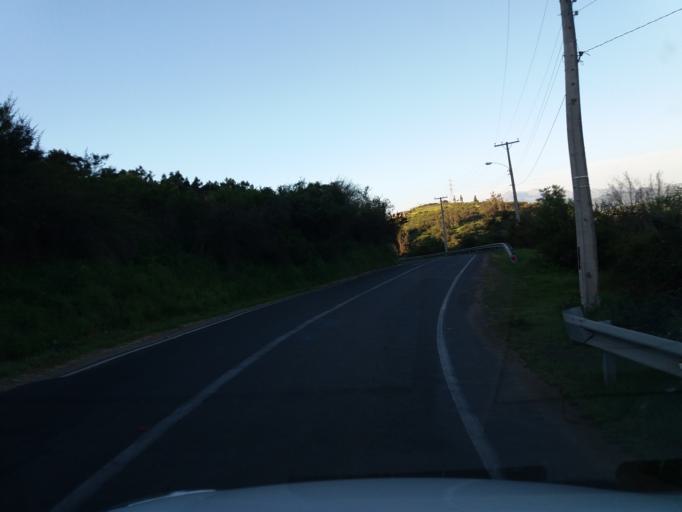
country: CL
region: Valparaiso
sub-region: Provincia de Quillota
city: Quillota
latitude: -32.8906
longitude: -71.2826
